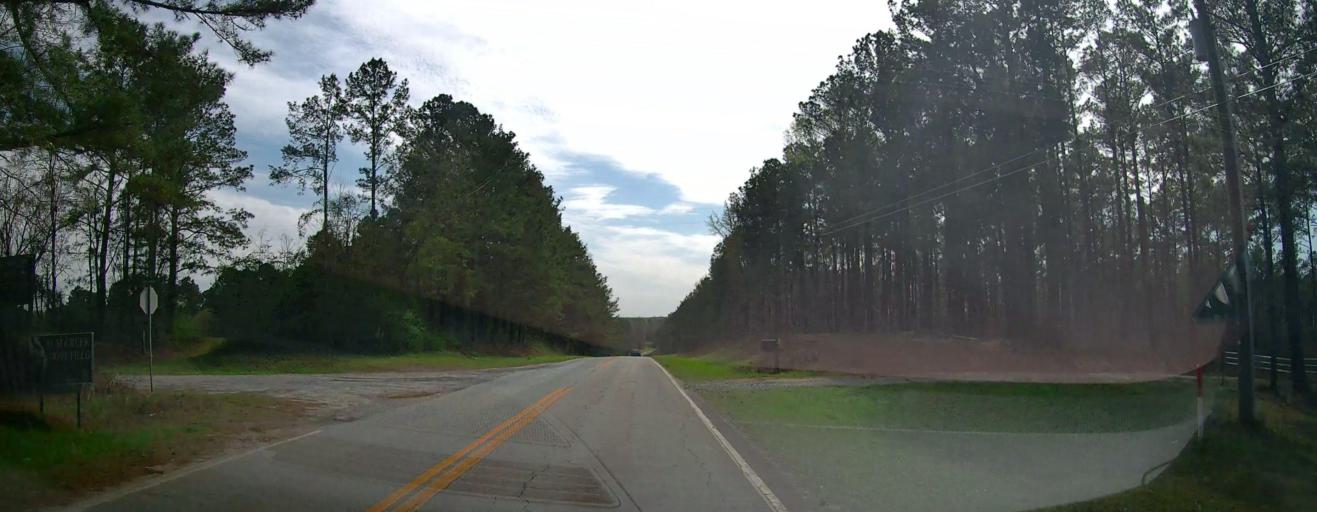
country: US
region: Georgia
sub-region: Monroe County
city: Forsyth
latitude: 33.0665
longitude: -83.8646
